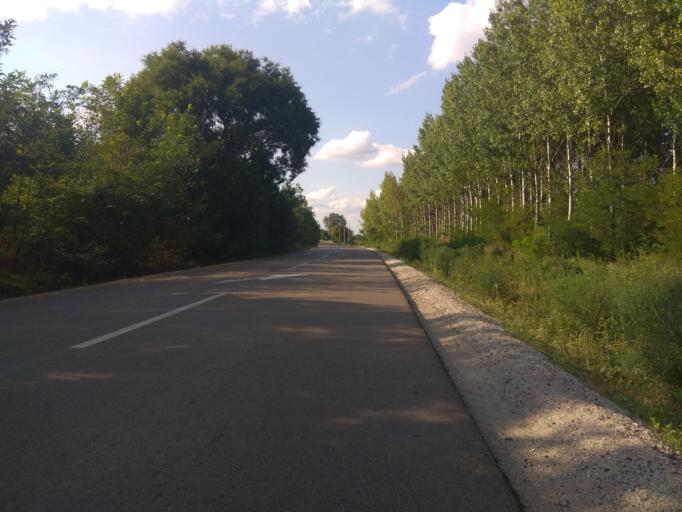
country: HU
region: Borsod-Abauj-Zemplen
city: Hejobaba
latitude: 47.8890
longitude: 20.8965
